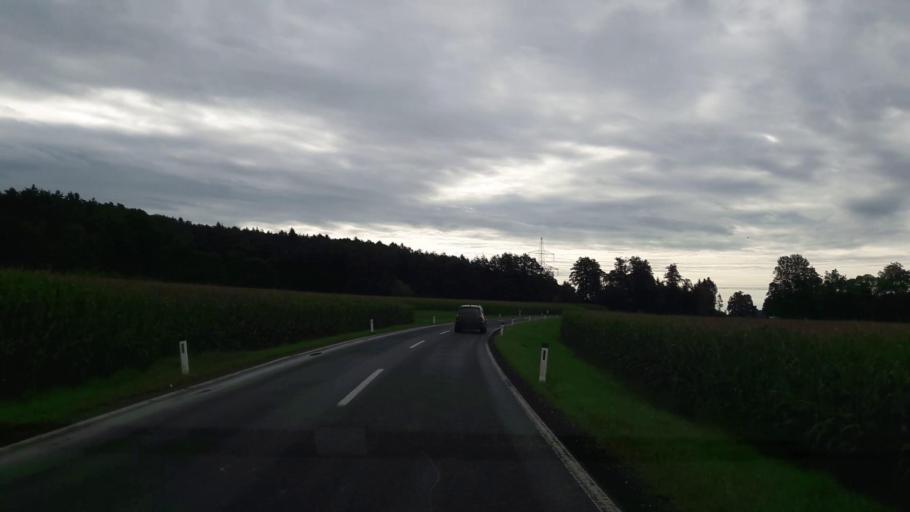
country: AT
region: Styria
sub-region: Politischer Bezirk Hartberg-Fuerstenfeld
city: Ebersdorf
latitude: 47.2081
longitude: 15.9432
